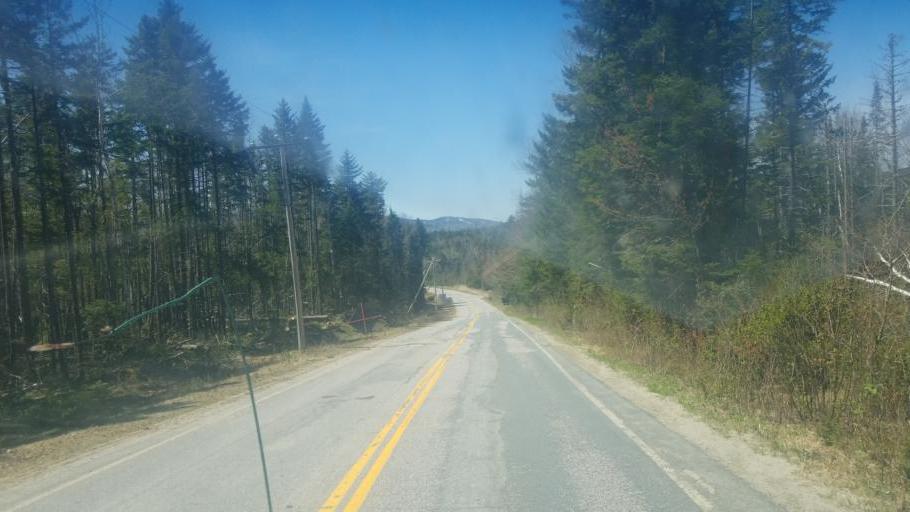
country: US
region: New Hampshire
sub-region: Coos County
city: Jefferson
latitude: 44.2640
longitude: -71.3797
